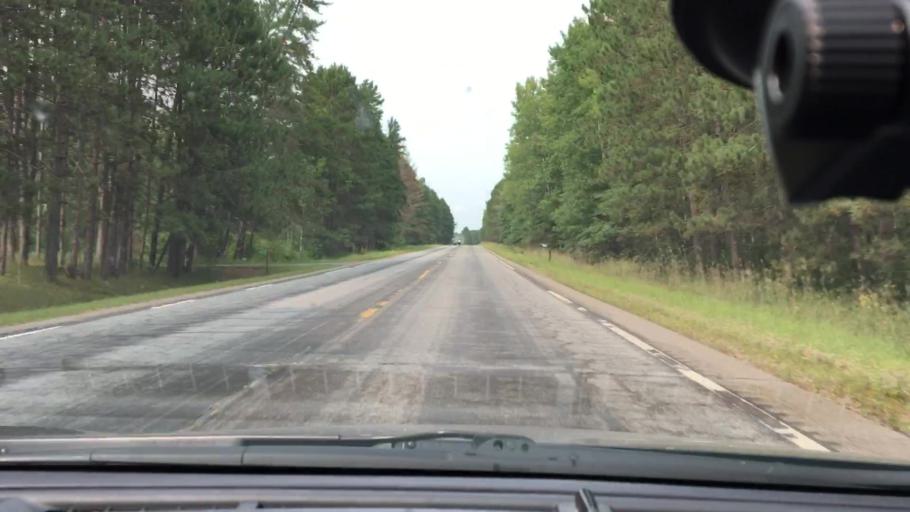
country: US
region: Minnesota
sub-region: Crow Wing County
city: Cross Lake
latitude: 46.7478
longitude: -93.9669
